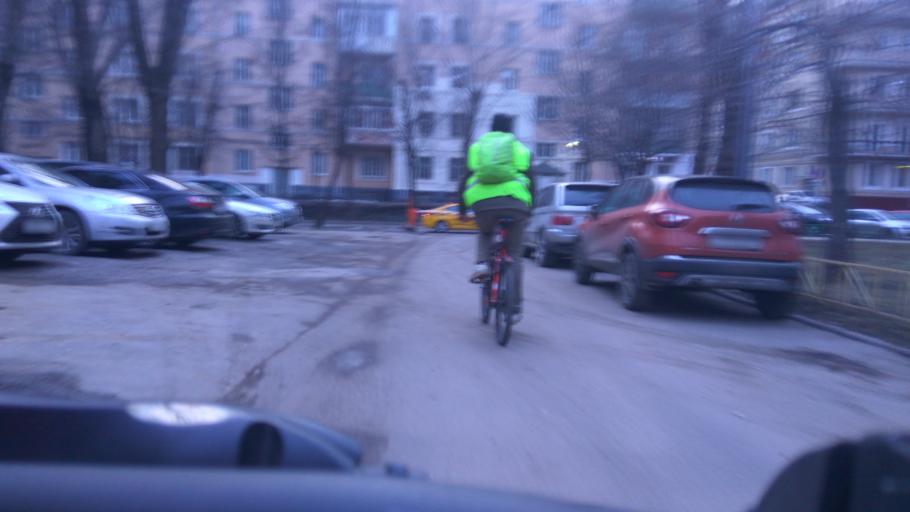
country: RU
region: Moskovskaya
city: Presnenskiy
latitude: 55.7575
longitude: 37.5539
